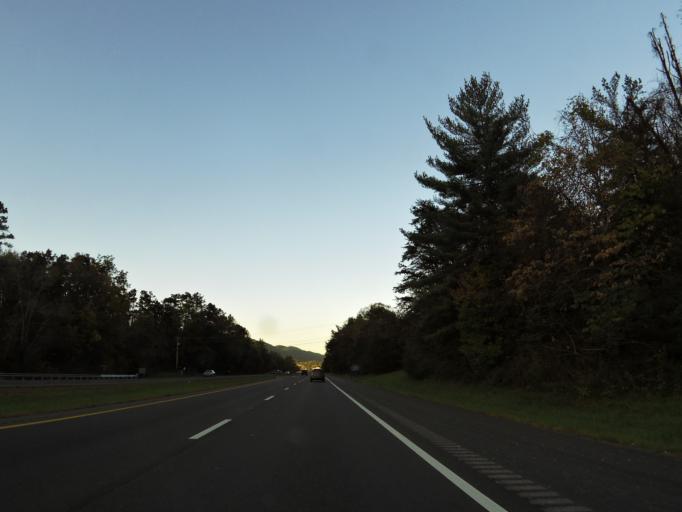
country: US
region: Tennessee
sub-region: Campbell County
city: Jacksboro
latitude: 36.3177
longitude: -84.2013
